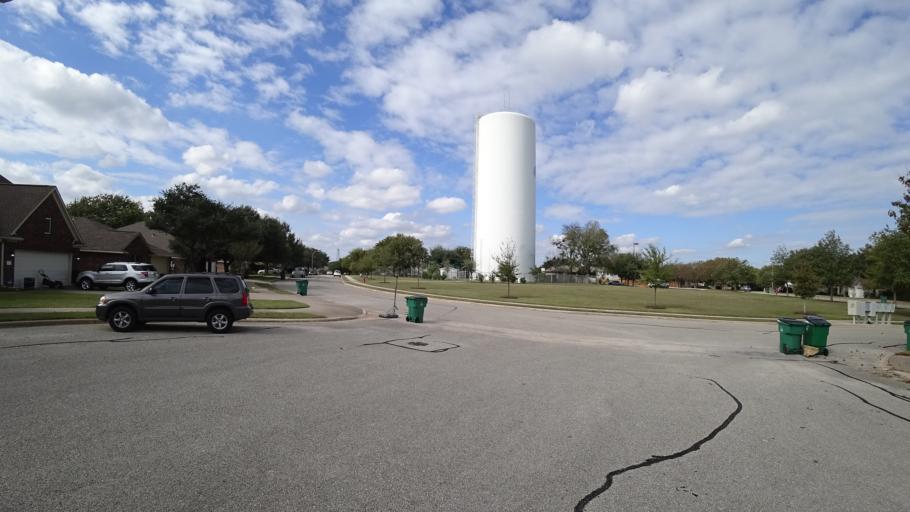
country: US
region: Texas
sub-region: Travis County
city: Pflugerville
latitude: 30.4386
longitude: -97.6413
